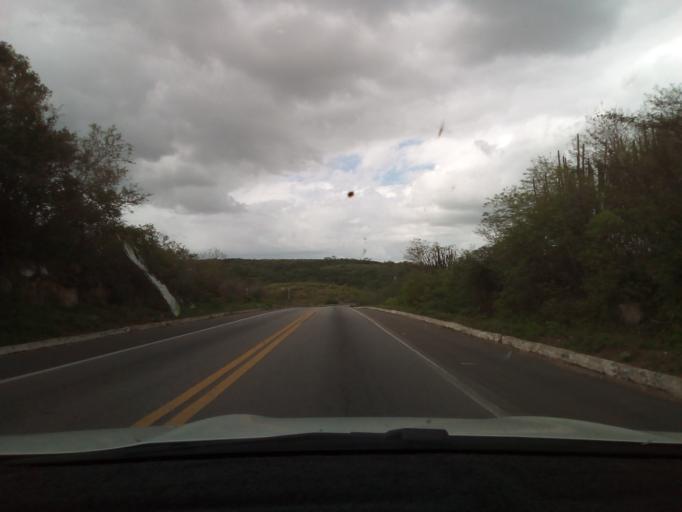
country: BR
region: Rio Grande do Norte
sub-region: Sao Paulo Do Potengi
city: Sao Paulo do Potengi
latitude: -5.7485
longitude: -35.9103
